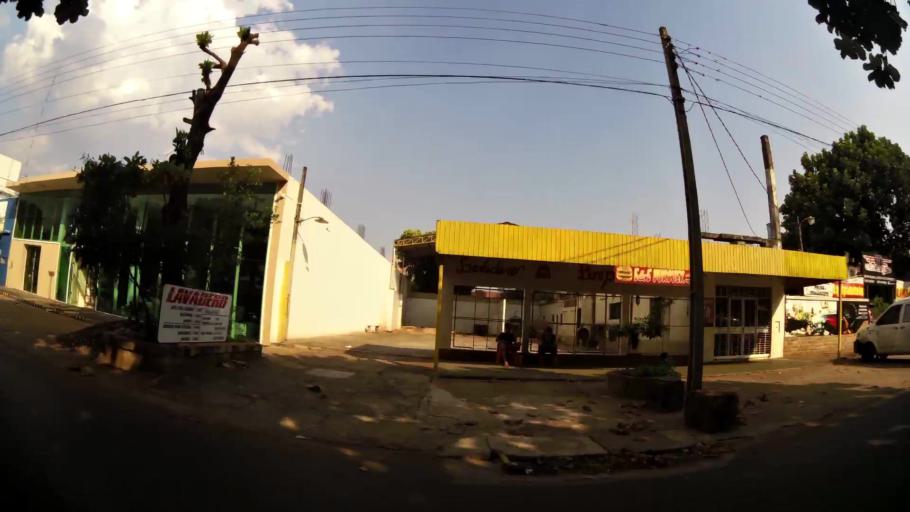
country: PY
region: Alto Parana
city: Presidente Franco
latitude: -25.5285
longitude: -54.6221
